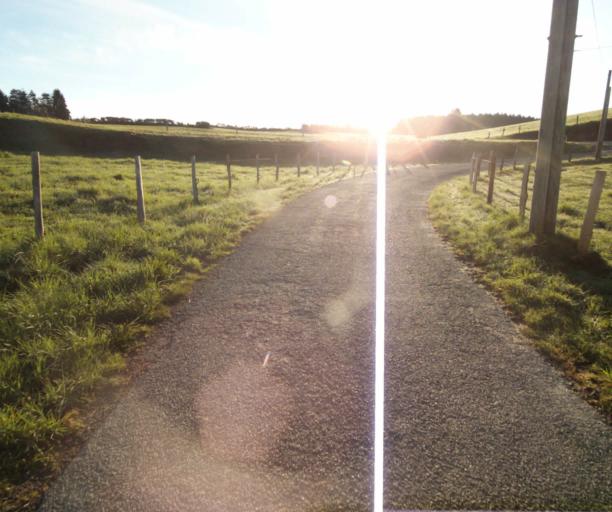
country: FR
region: Limousin
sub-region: Departement de la Correze
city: Correze
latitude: 45.3774
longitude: 1.8554
